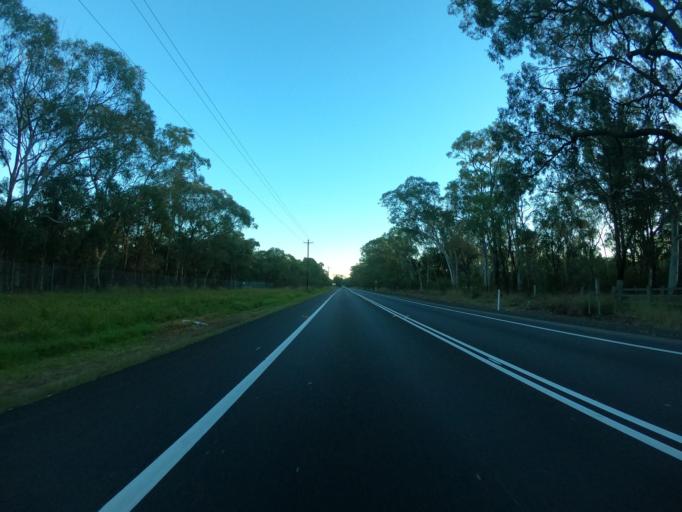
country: AU
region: New South Wales
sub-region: Hawkesbury
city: South Windsor
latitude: -33.6550
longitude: 150.7940
